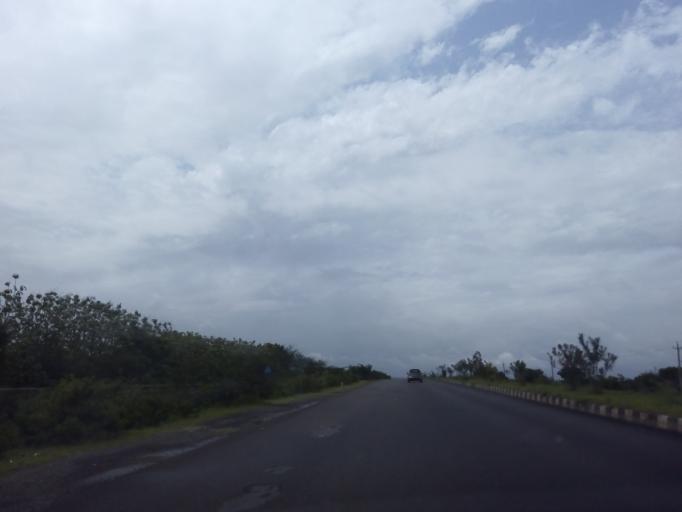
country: IN
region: Karnataka
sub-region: Haveri
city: Byadgi
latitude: 14.7040
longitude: 75.5194
